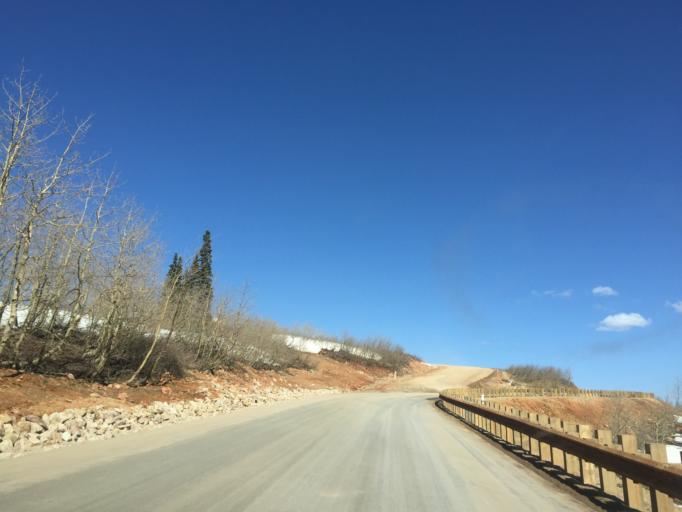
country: US
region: Utah
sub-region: Weber County
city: Wolf Creek
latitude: 41.3680
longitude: -111.7679
